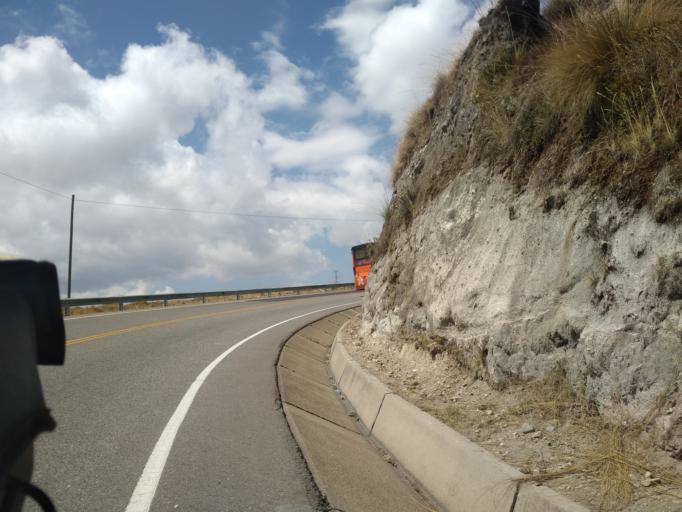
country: PE
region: La Libertad
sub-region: Provincia de Santiago de Chuco
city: Quiruvilca
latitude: -7.9208
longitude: -78.1522
